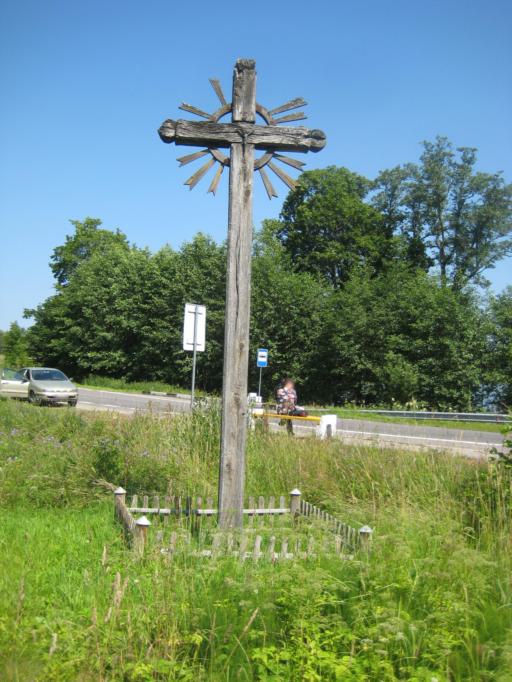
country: LT
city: Dukstas
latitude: 55.5456
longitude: 26.3211
